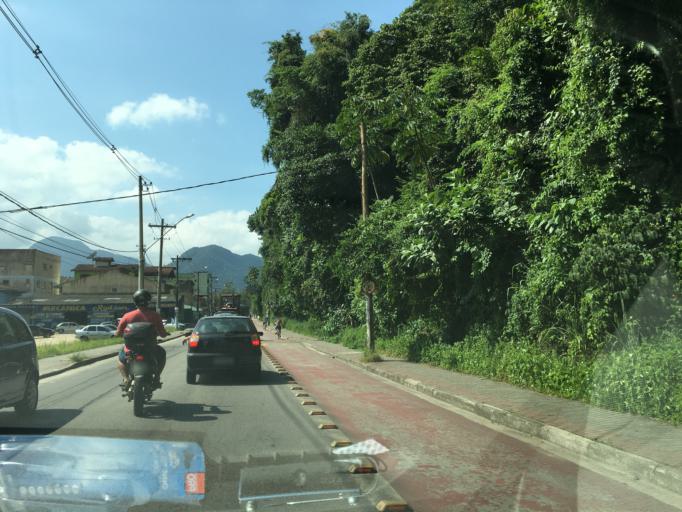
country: BR
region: Sao Paulo
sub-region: Ubatuba
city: Ubatuba
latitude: -23.4311
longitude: -45.0681
